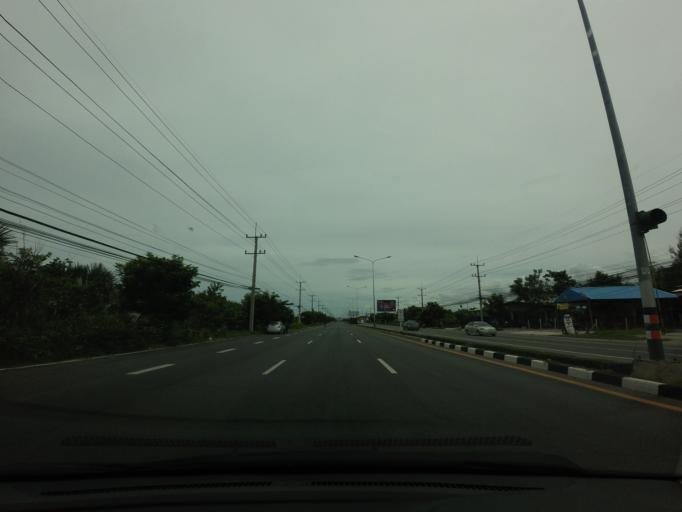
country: TH
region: Phetchaburi
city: Cha-am
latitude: 12.6981
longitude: 99.9532
